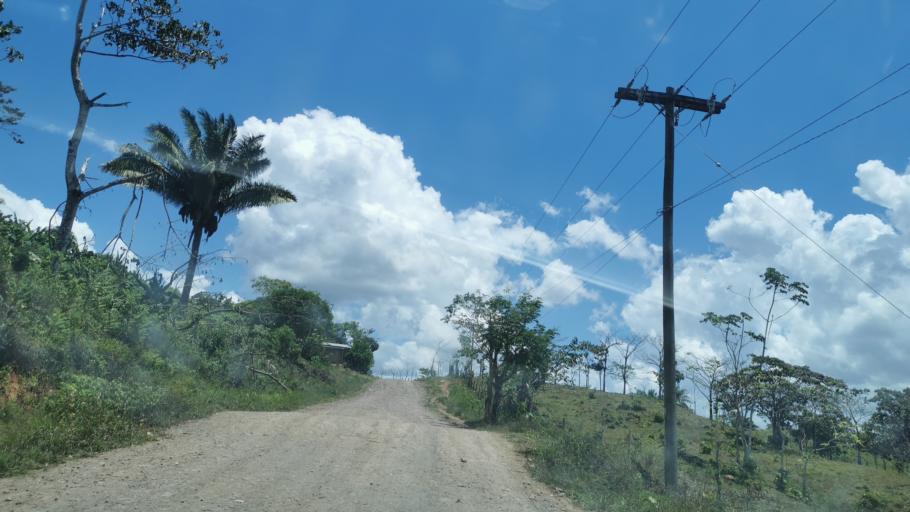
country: NI
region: Atlantico Sur
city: Rama
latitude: 12.3917
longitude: -84.3090
